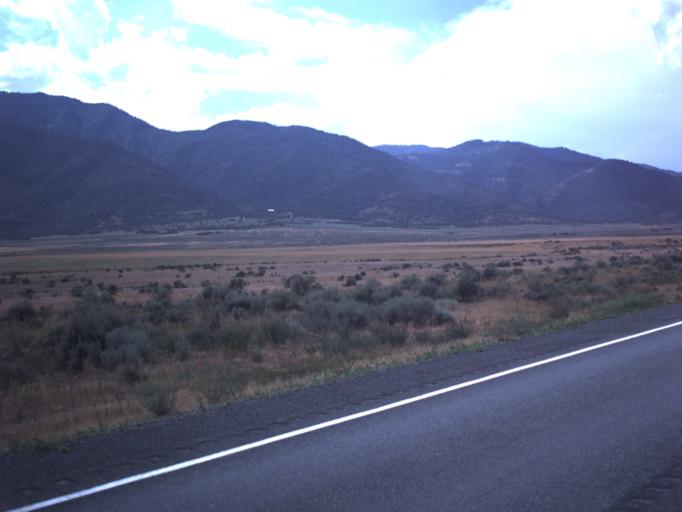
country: US
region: Utah
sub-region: Sanpete County
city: Fountain Green
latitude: 39.6474
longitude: -111.6438
